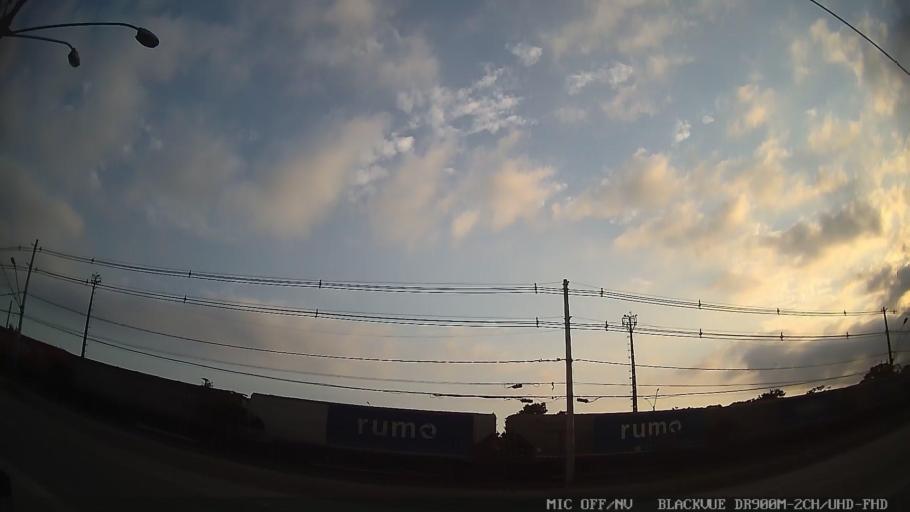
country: BR
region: Sao Paulo
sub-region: Guaruja
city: Guaruja
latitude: -23.9701
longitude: -46.2787
